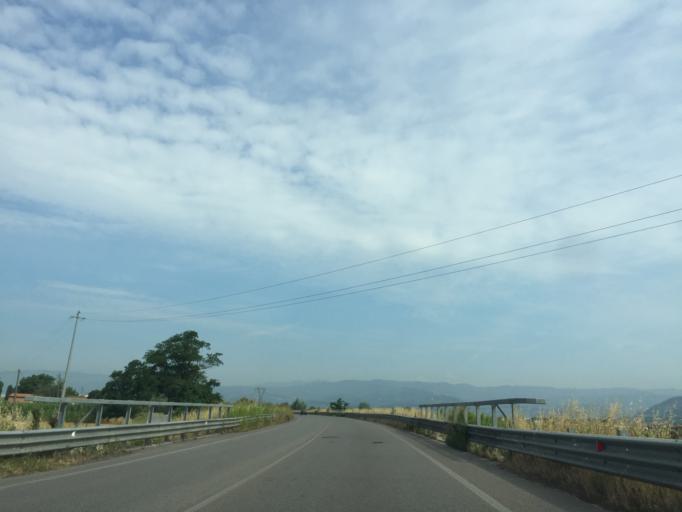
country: IT
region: Tuscany
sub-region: Provincia di Pistoia
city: Uggia-Pazzera-Bizzarrino
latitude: 43.8346
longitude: 10.8267
